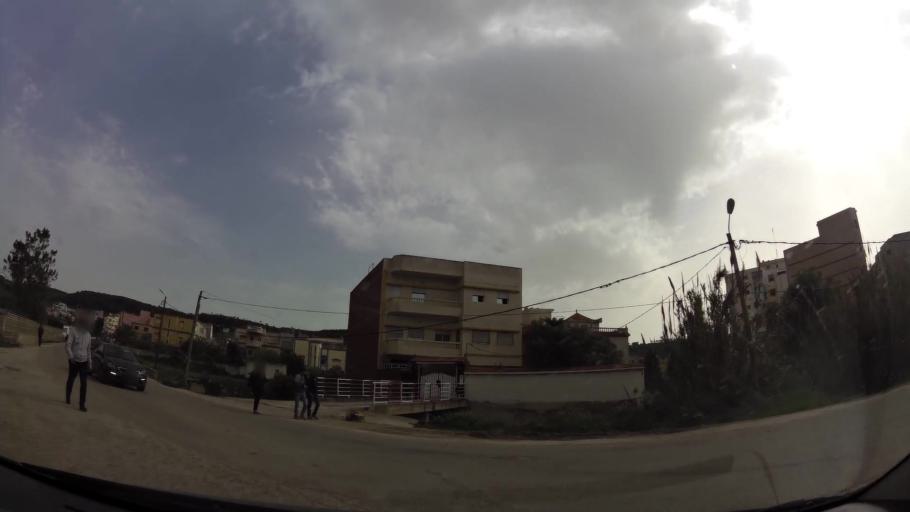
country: MA
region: Tanger-Tetouan
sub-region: Tanger-Assilah
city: Boukhalef
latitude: 35.7047
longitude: -5.9016
